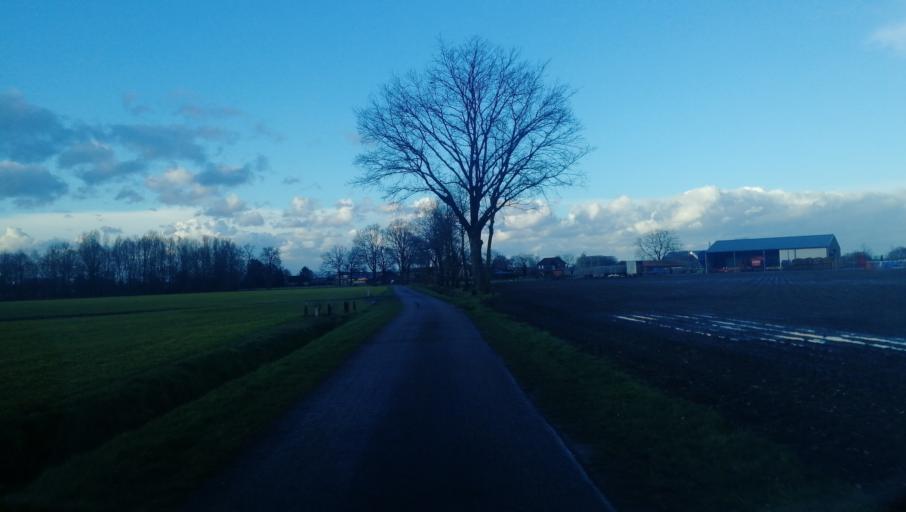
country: NL
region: Limburg
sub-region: Gemeente Peel en Maas
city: Maasbree
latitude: 51.3462
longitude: 6.0432
